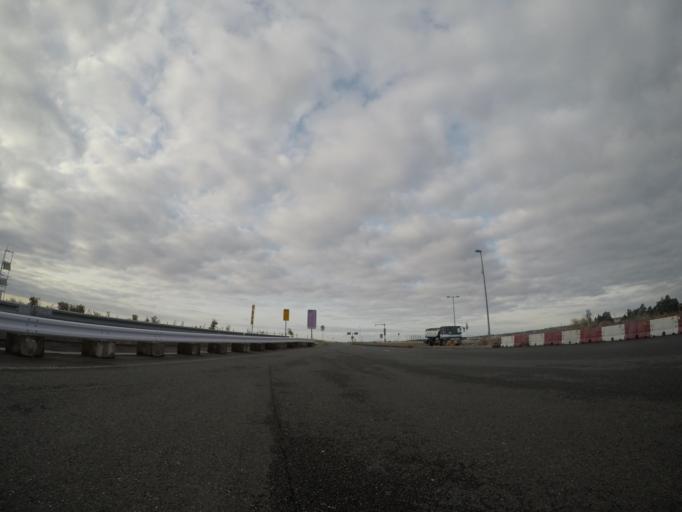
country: JP
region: Shizuoka
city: Hamakita
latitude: 34.8314
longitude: 137.8139
